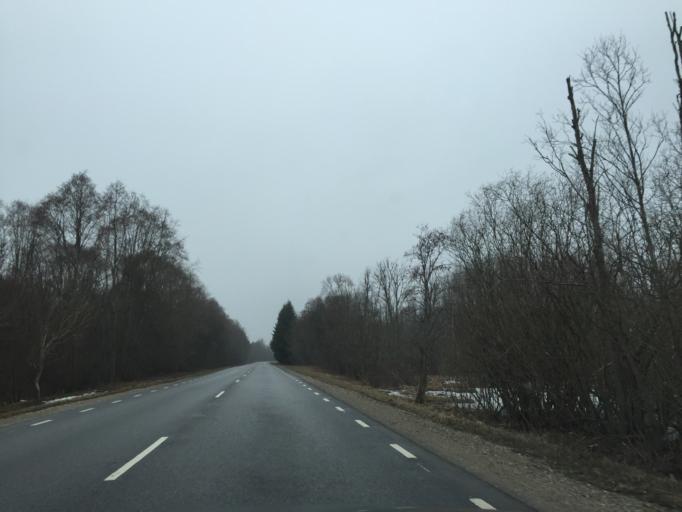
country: EE
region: Laeaene
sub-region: Lihula vald
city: Lihula
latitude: 58.5931
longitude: 23.7092
